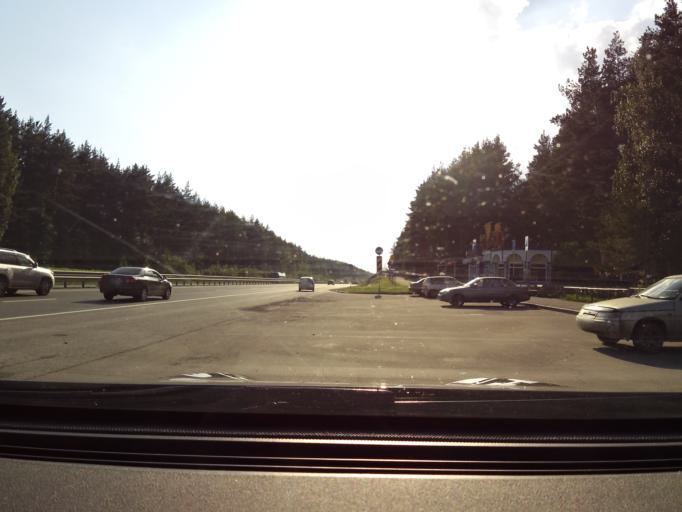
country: RU
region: Sverdlovsk
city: Severka
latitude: 56.8320
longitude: 60.3536
